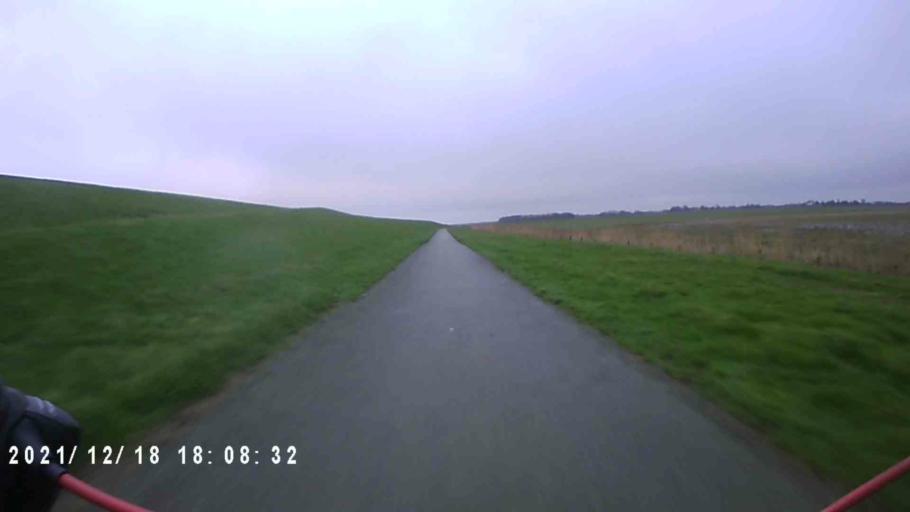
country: NL
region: Friesland
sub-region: Gemeente Dongeradeel
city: Holwerd
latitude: 53.3855
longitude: 5.9243
